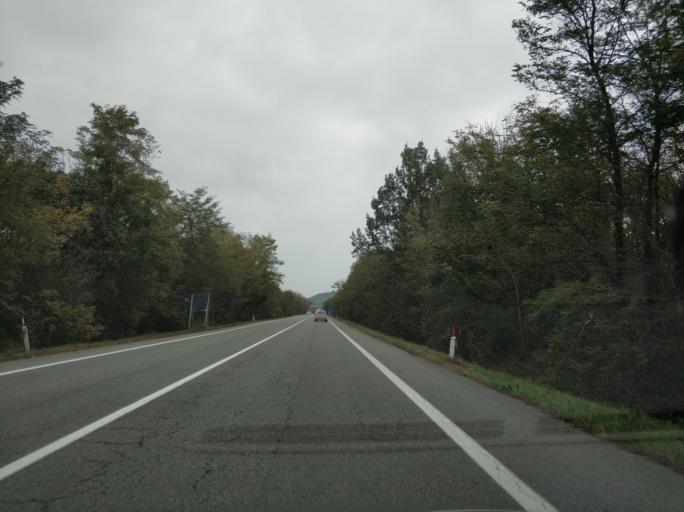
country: IT
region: Piedmont
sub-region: Provincia di Torino
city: Bairo
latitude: 45.3887
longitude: 7.7404
